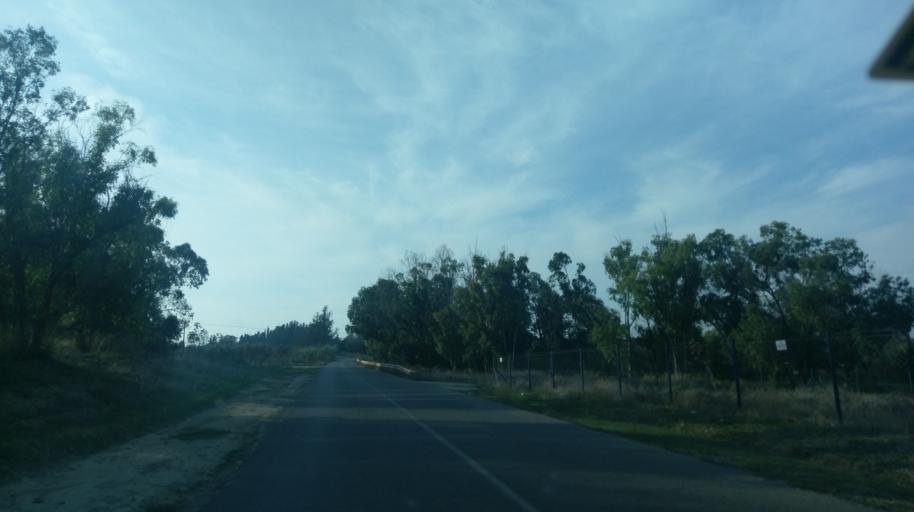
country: CY
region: Ammochostos
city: Achna
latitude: 35.1064
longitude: 33.7613
